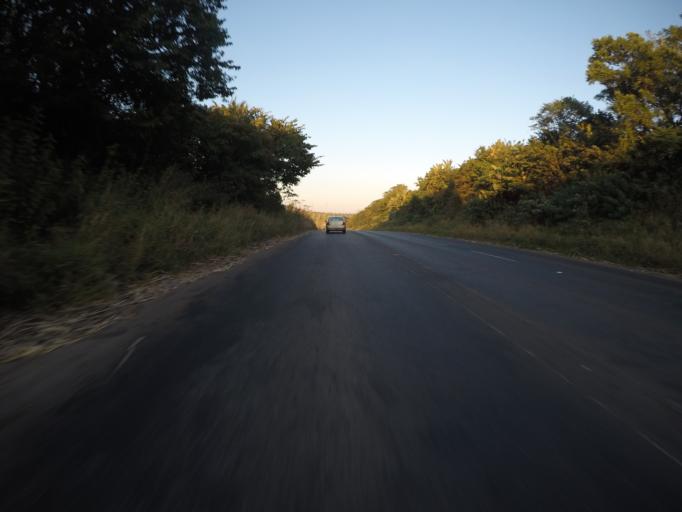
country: ZA
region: KwaZulu-Natal
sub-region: uThungulu District Municipality
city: eSikhawini
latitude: -28.8171
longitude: 31.8867
